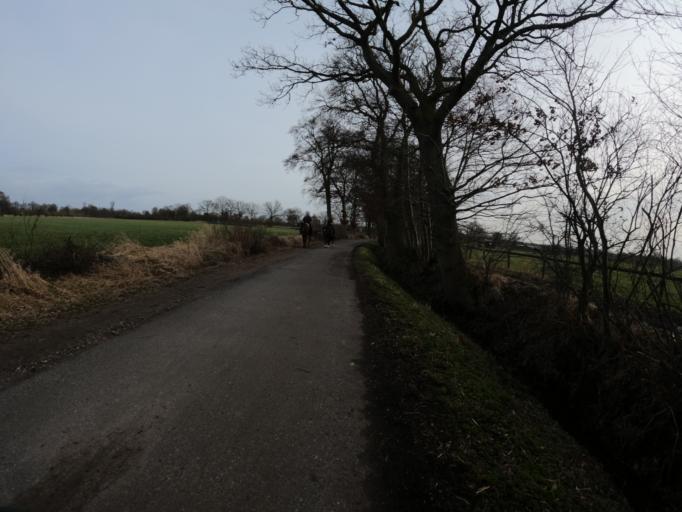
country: DE
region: Schleswig-Holstein
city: Rellingen
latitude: 53.5959
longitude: 9.7974
